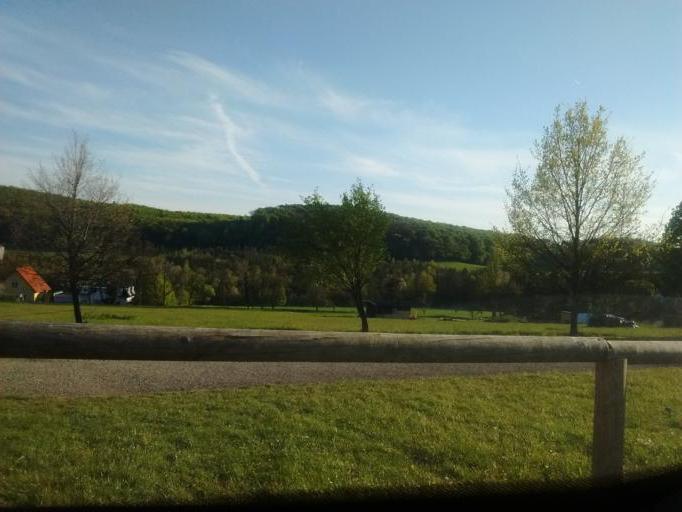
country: AT
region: Lower Austria
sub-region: Politischer Bezirk Modling
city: Gaaden
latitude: 48.0760
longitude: 16.1873
